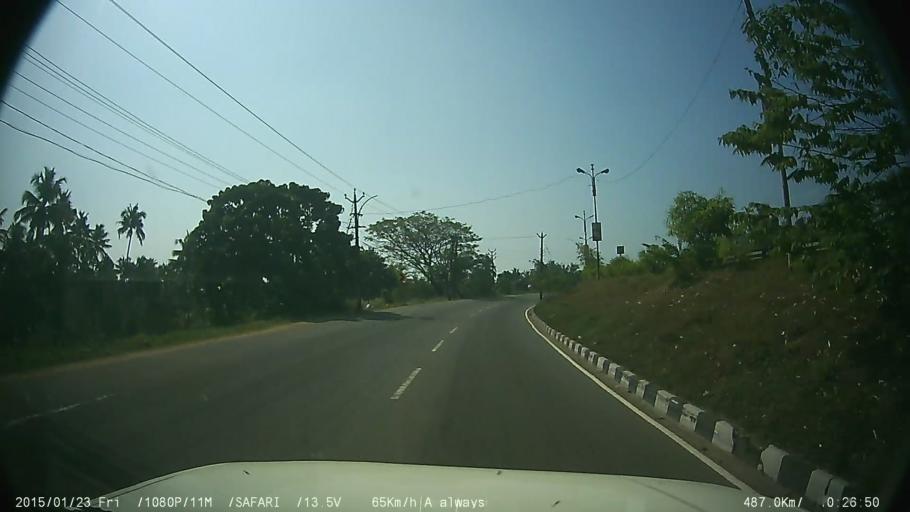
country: IN
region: Kerala
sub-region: Ernakulam
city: Angamali
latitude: 10.1814
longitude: 76.3797
